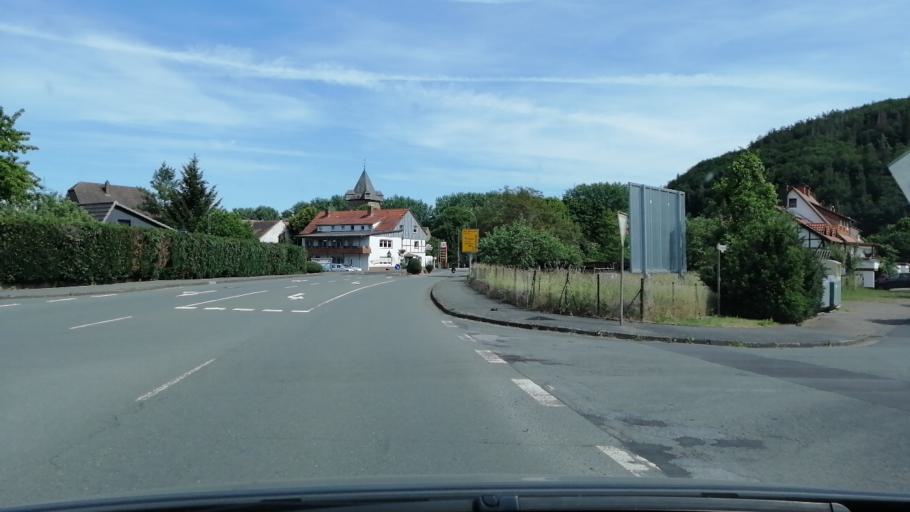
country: DE
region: Hesse
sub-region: Regierungsbezirk Kassel
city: Waldeck
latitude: 51.1677
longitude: 9.0844
